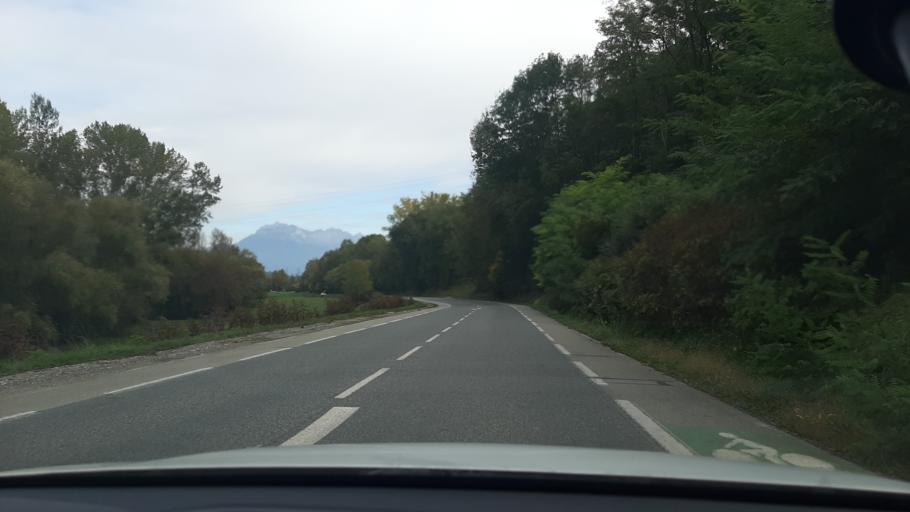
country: FR
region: Rhone-Alpes
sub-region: Departement de l'Isere
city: Pontcharra
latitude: 45.4532
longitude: 6.0451
